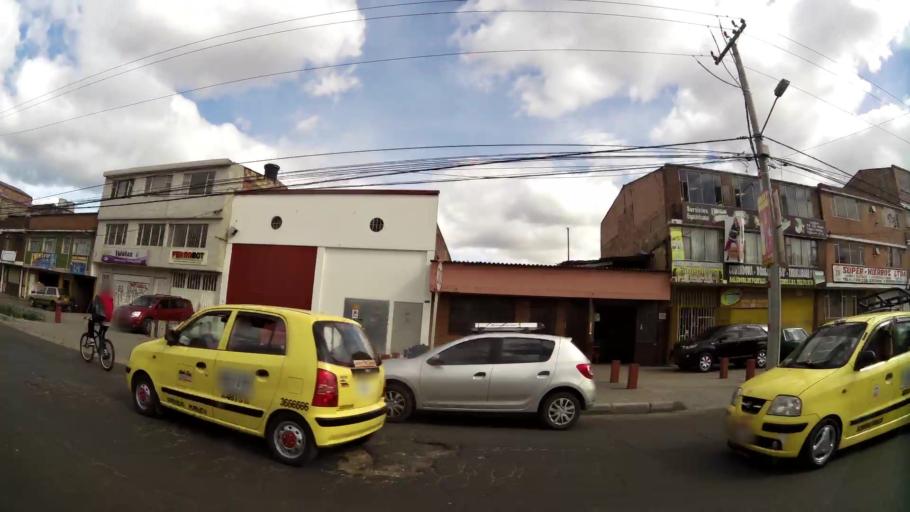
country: CO
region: Bogota D.C.
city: Bogota
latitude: 4.6123
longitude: -74.1392
